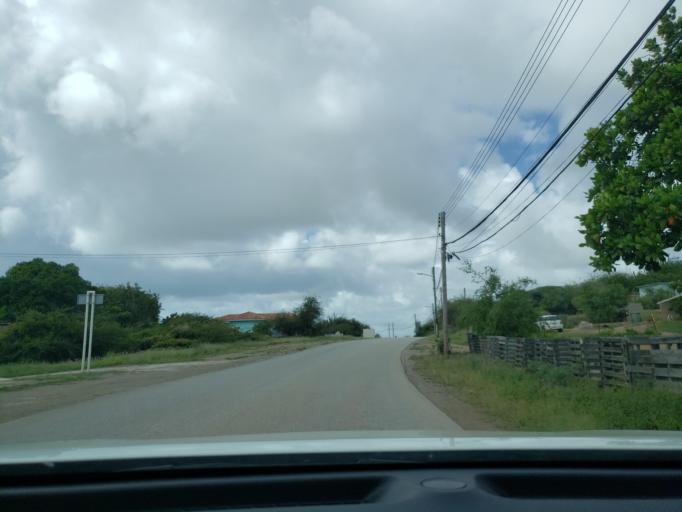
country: CW
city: Willemstad
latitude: 12.0929
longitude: -68.8698
